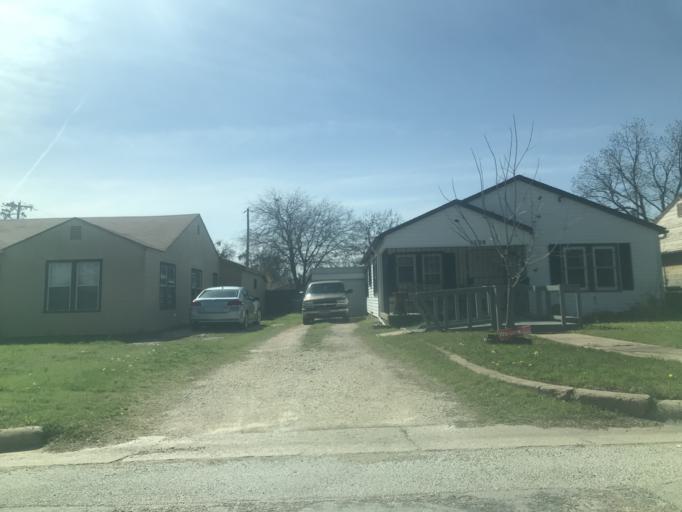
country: US
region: Texas
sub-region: Taylor County
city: Abilene
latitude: 32.4690
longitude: -99.7380
